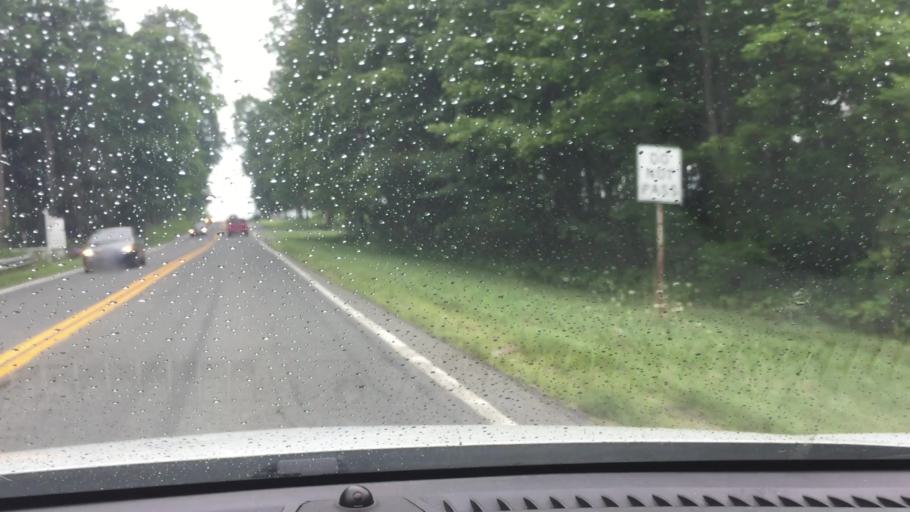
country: US
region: Massachusetts
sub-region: Berkshire County
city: Lenox
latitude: 42.3270
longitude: -73.2881
